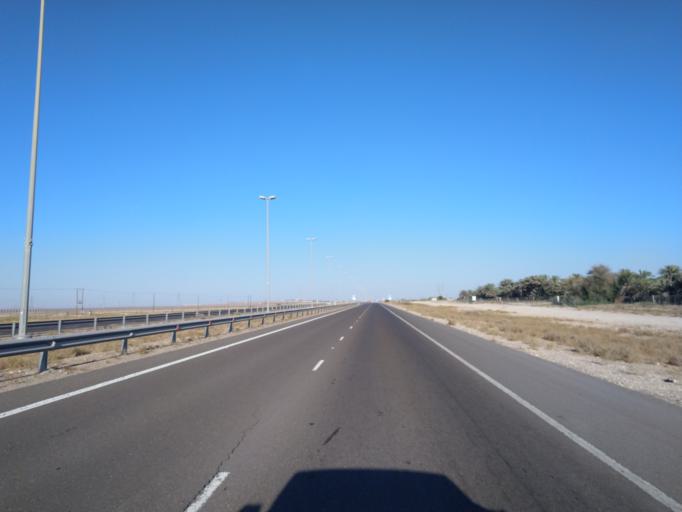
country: OM
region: Al Buraimi
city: Al Buraymi
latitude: 24.4924
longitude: 55.4132
